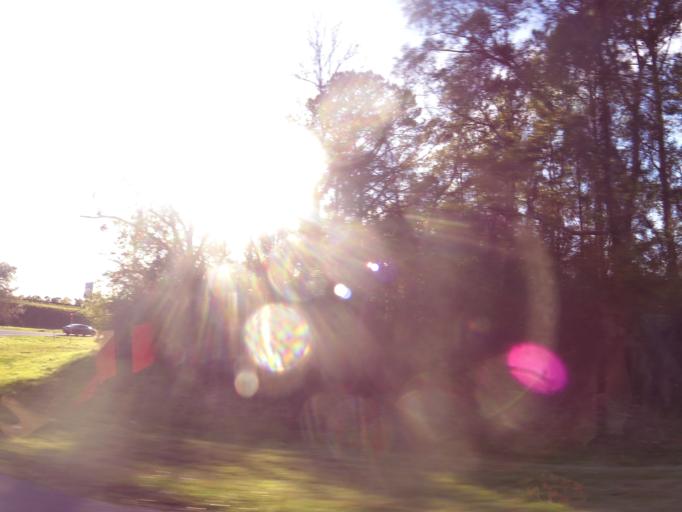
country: US
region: Florida
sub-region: Duval County
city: Jacksonville
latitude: 30.4499
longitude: -81.6132
